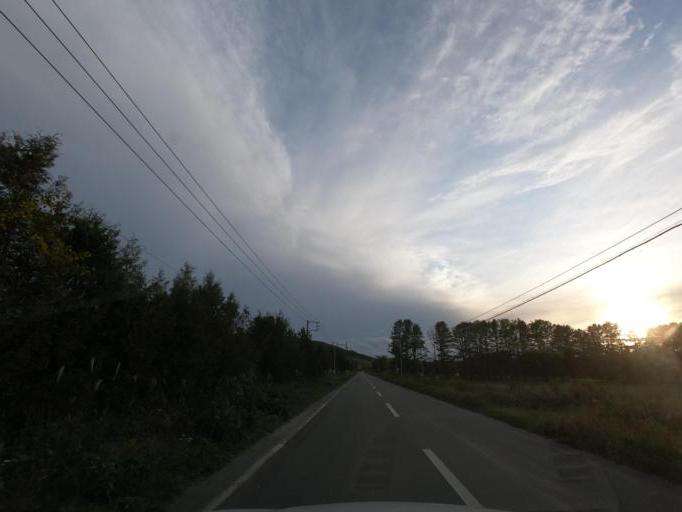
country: JP
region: Hokkaido
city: Obihiro
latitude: 42.5722
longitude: 143.3205
